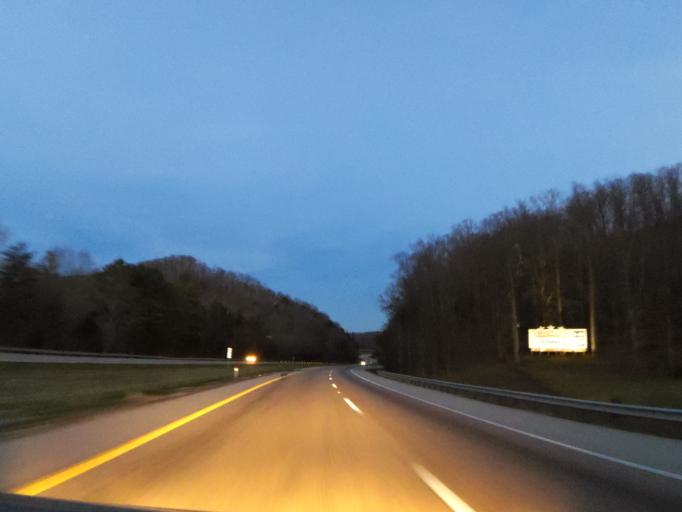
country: US
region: Tennessee
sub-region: Loudon County
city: Lenoir City
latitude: 35.8713
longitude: -84.2661
